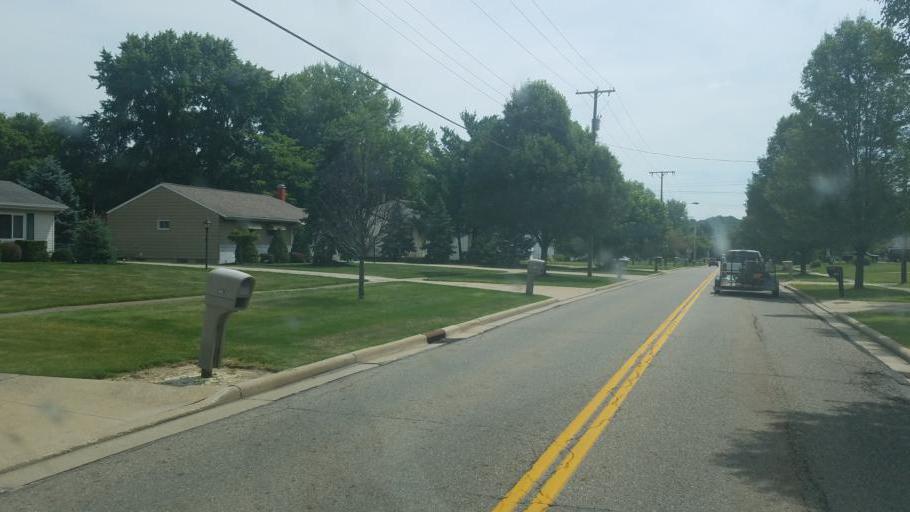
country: US
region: Ohio
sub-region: Summit County
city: Twinsburg
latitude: 41.3403
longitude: -81.4629
